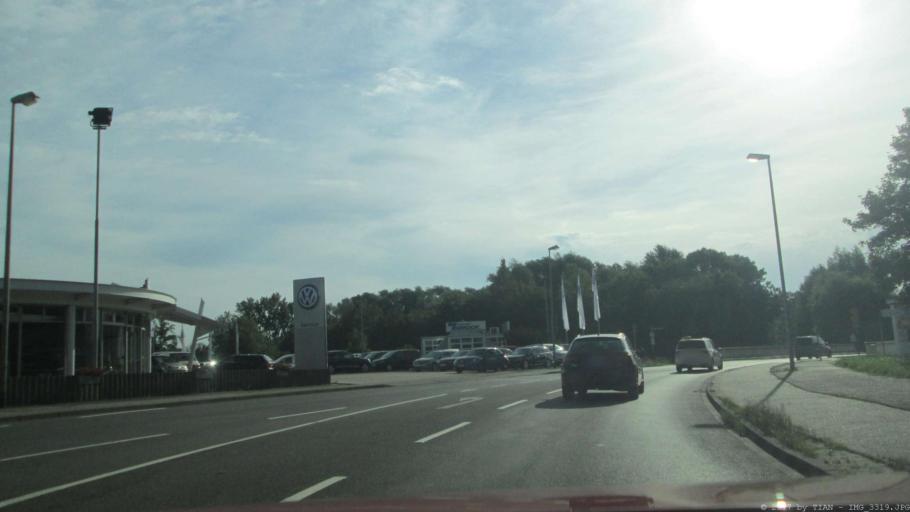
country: DE
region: Lower Saxony
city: Wolfsburg
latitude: 52.4380
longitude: 10.8421
